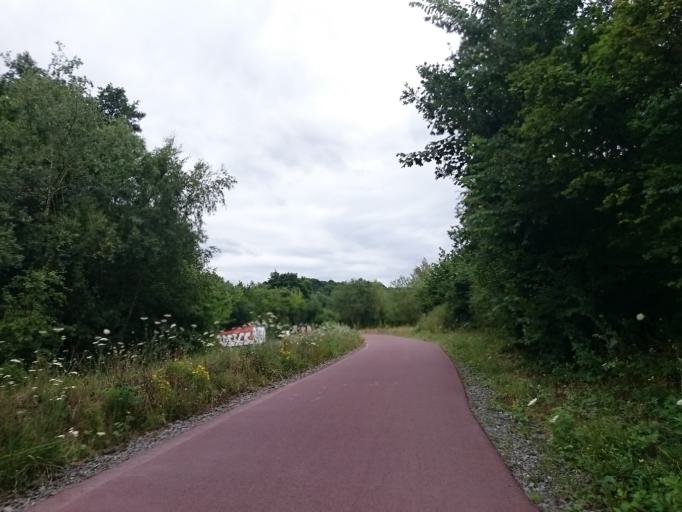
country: FR
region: Lower Normandy
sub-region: Departement du Calvados
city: May-sur-Orne
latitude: 49.1060
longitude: -0.3849
